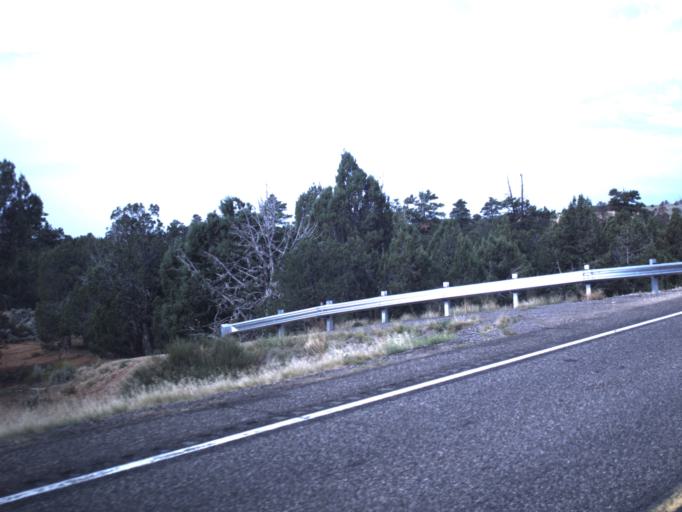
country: US
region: Utah
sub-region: Kane County
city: Kanab
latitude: 37.2213
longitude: -112.7122
